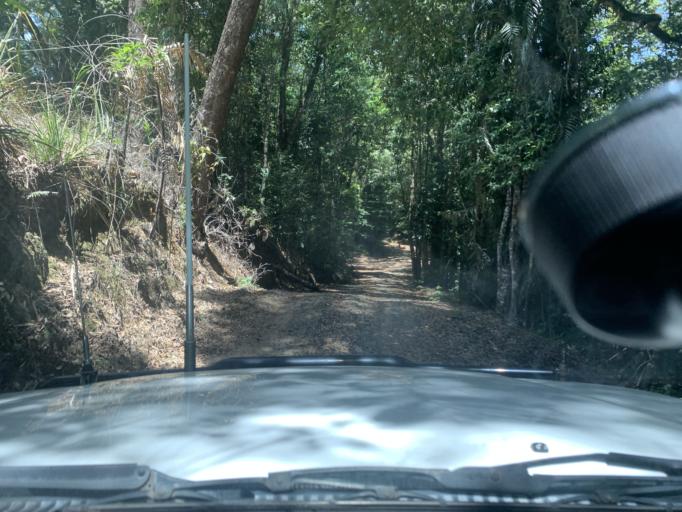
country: AU
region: Queensland
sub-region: Cairns
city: Woree
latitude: -16.9768
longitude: 145.6559
